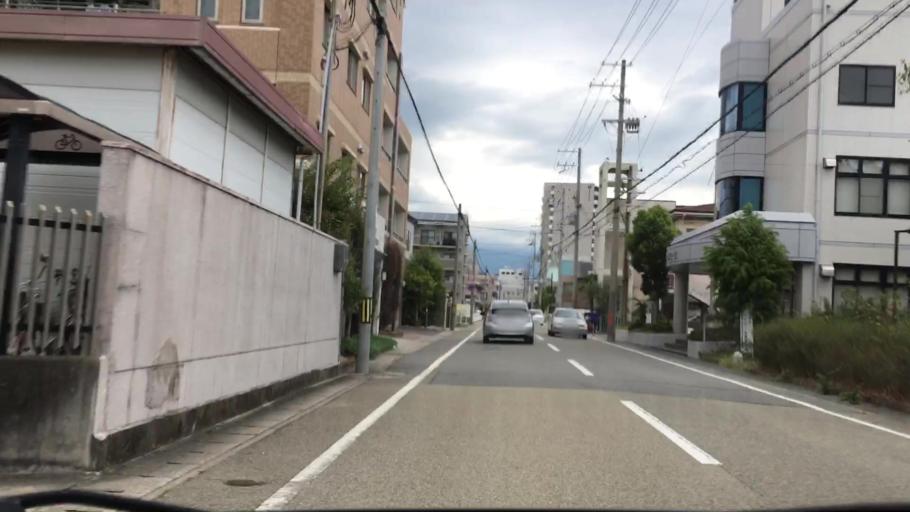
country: JP
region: Hyogo
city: Himeji
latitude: 34.8192
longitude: 134.6931
